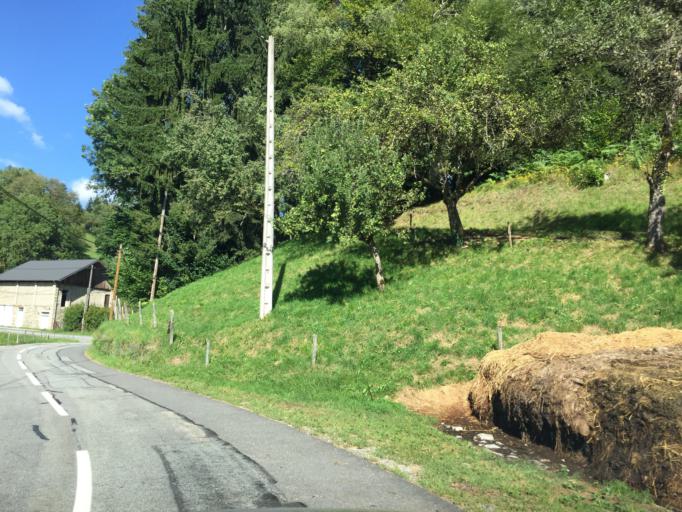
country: FR
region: Rhone-Alpes
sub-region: Departement de la Savoie
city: La Rochette
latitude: 45.4633
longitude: 6.1683
